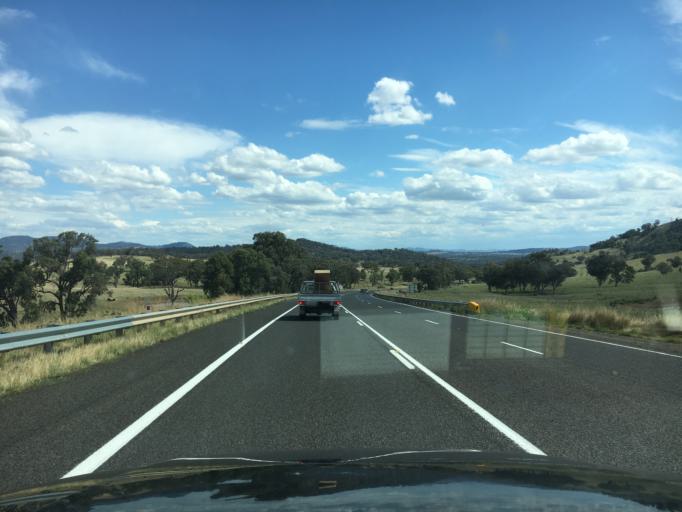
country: AU
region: New South Wales
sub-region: Liverpool Plains
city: Quirindi
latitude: -31.5053
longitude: 150.8615
